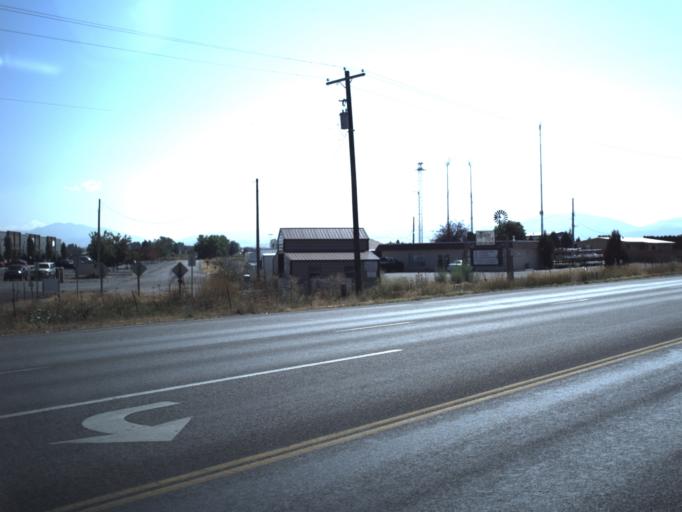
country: US
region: Utah
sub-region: Cache County
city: Nibley
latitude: 41.7028
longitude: -111.8526
